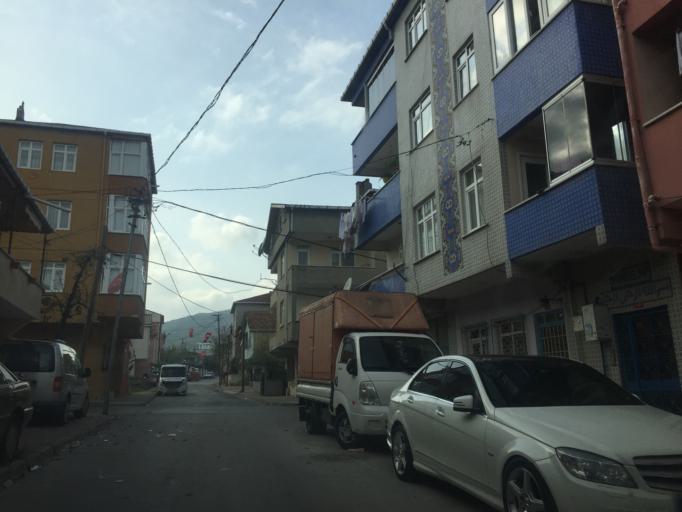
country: TR
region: Istanbul
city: Sultanbeyli
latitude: 40.9368
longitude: 29.2868
